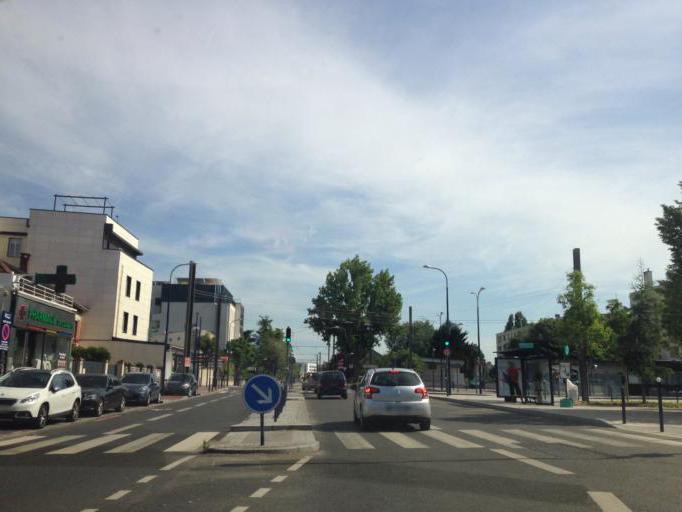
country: FR
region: Ile-de-France
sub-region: Departement des Hauts-de-Seine
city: Meudon
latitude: 48.7855
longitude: 2.2377
